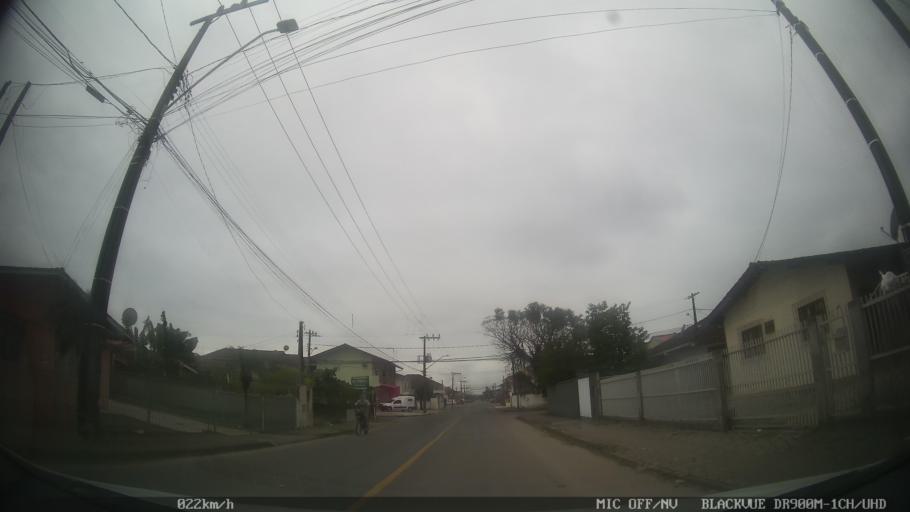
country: BR
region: Santa Catarina
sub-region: Joinville
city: Joinville
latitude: -26.3204
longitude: -48.8184
